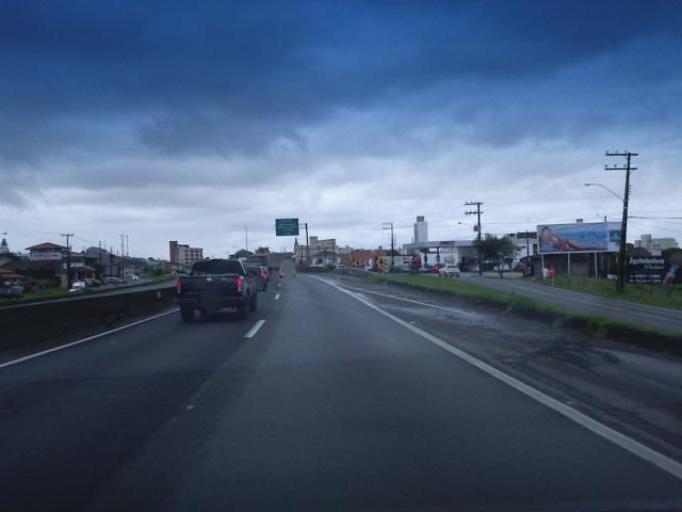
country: BR
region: Santa Catarina
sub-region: Barra Velha
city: Barra Velha
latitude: -26.6496
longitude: -48.6868
